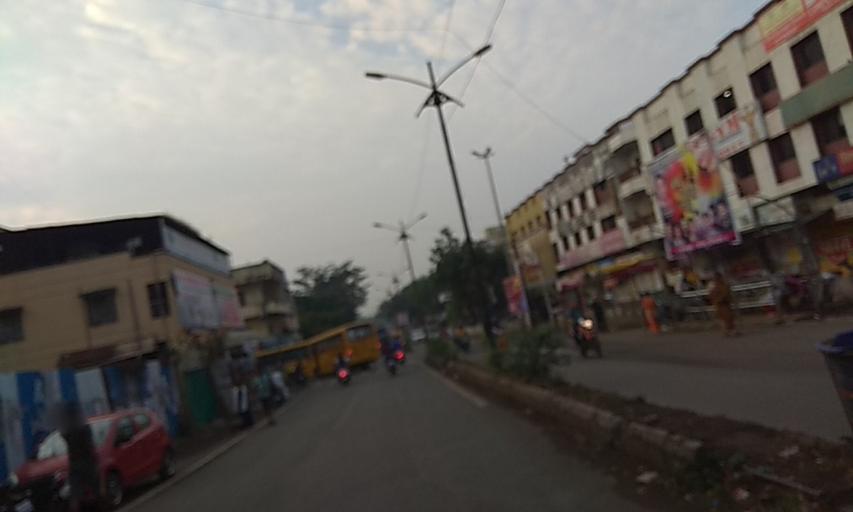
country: IN
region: Maharashtra
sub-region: Pune Division
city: Lohogaon
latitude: 18.5599
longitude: 73.9280
